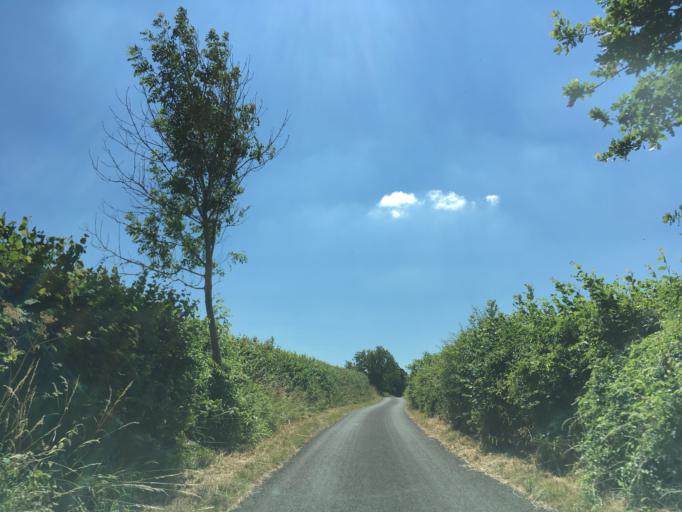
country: GB
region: England
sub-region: Wiltshire
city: Luckington
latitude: 51.5565
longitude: -2.2197
